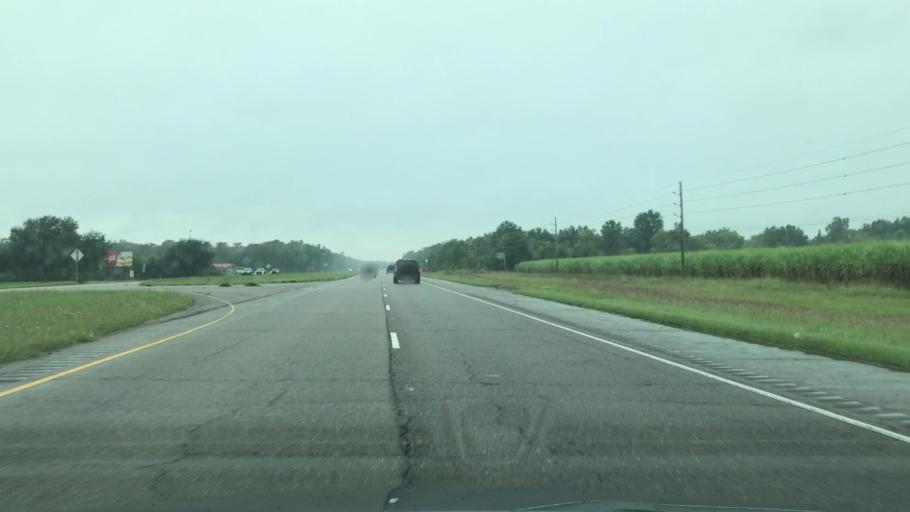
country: US
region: Louisiana
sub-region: Lafourche Parish
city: Raceland
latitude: 29.7399
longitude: -90.5574
